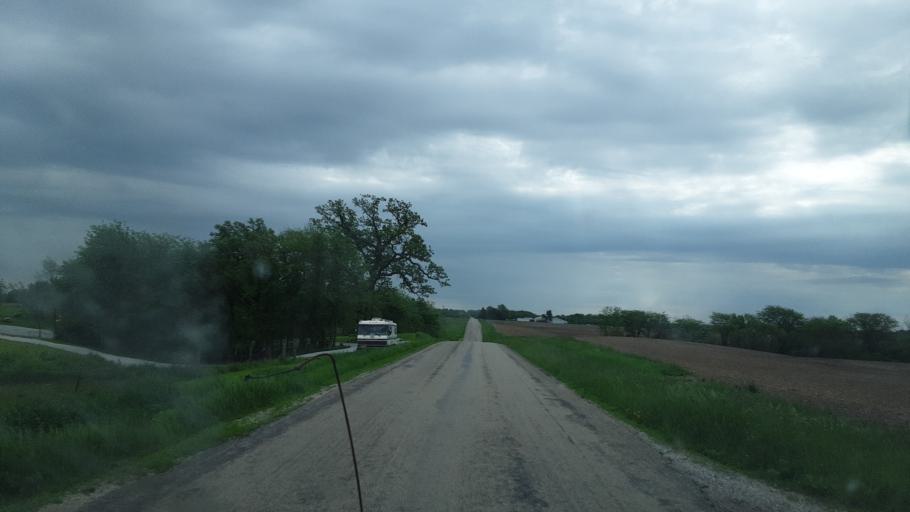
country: US
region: Illinois
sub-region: Fulton County
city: Astoria
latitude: 40.3645
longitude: -90.4685
